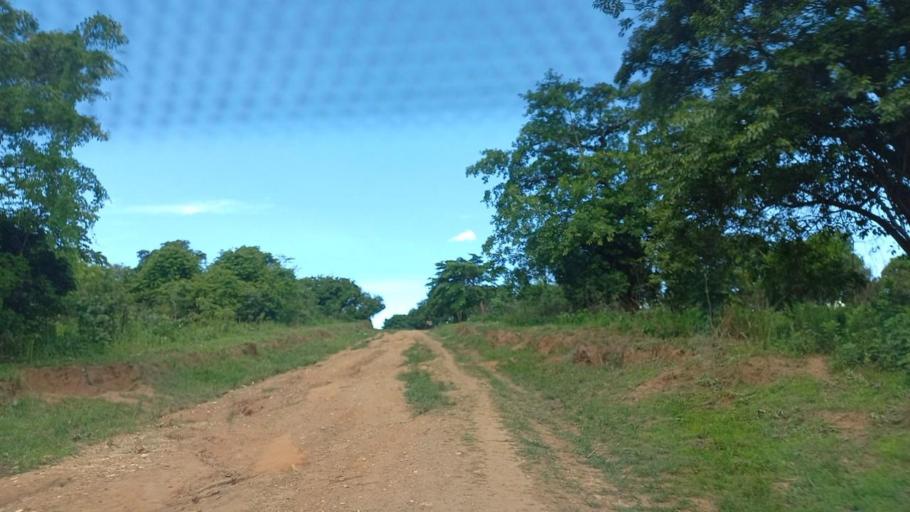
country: ZM
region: North-Western
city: Mwinilunga
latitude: -12.3593
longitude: 24.2323
